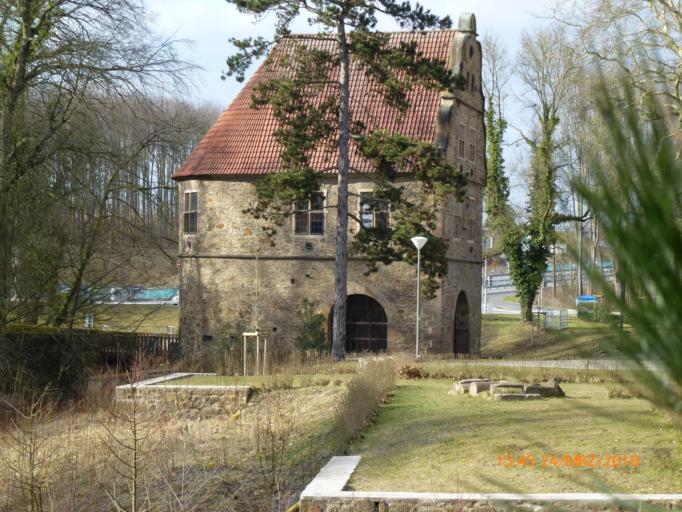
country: DE
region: North Rhine-Westphalia
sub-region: Regierungsbezirk Arnsberg
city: Dortmund
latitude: 51.4815
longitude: 7.4691
